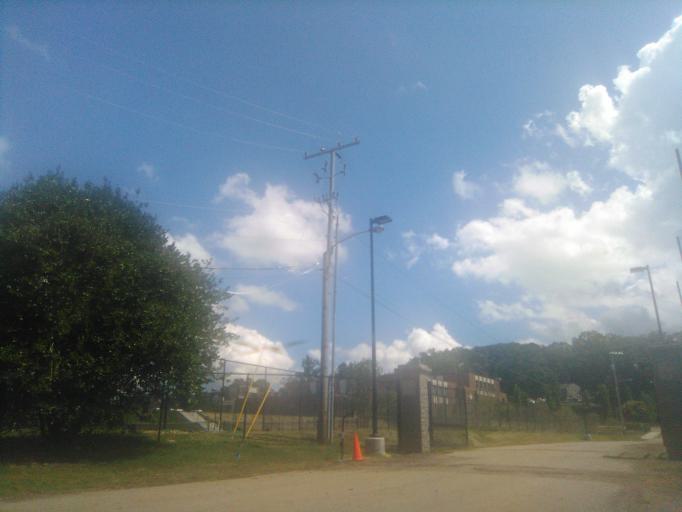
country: US
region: Tennessee
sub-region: Davidson County
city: Belle Meade
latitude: 36.1035
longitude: -86.8427
